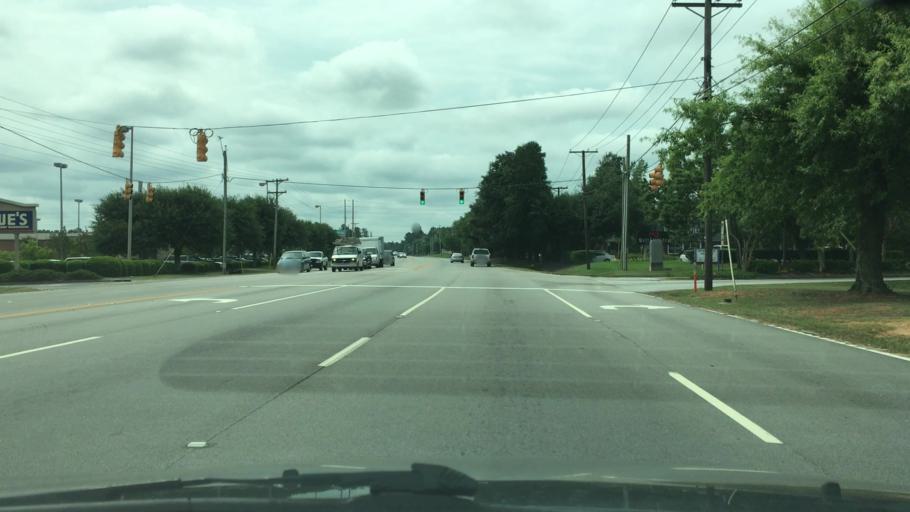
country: US
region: South Carolina
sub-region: Aiken County
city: Aiken
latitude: 33.5093
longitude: -81.7122
